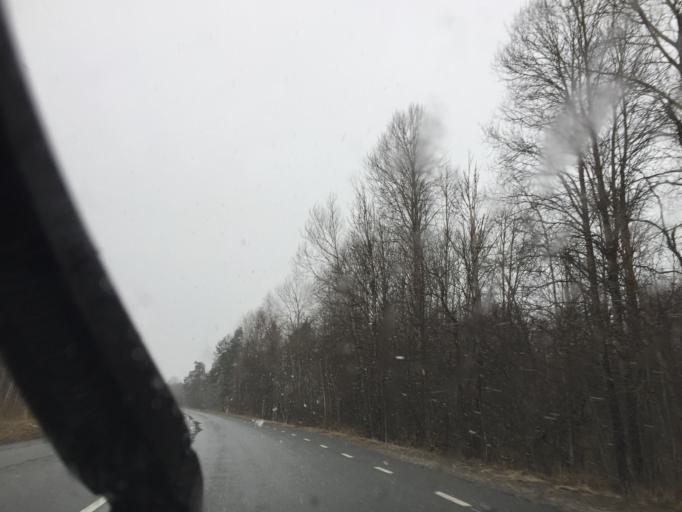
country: EE
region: Laeaene
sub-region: Ridala Parish
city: Uuemoisa
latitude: 58.8303
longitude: 23.7047
